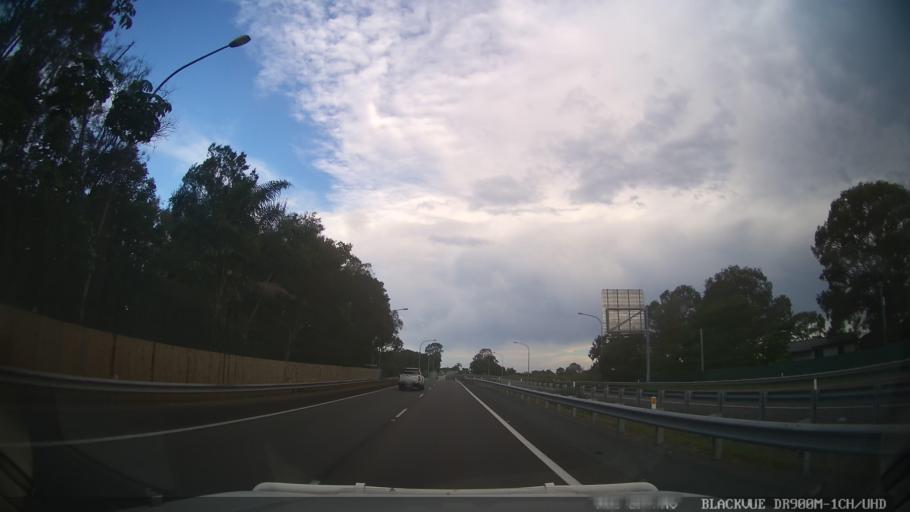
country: AU
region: Queensland
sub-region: Sunshine Coast
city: Mooloolaba
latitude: -26.6949
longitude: 153.1127
